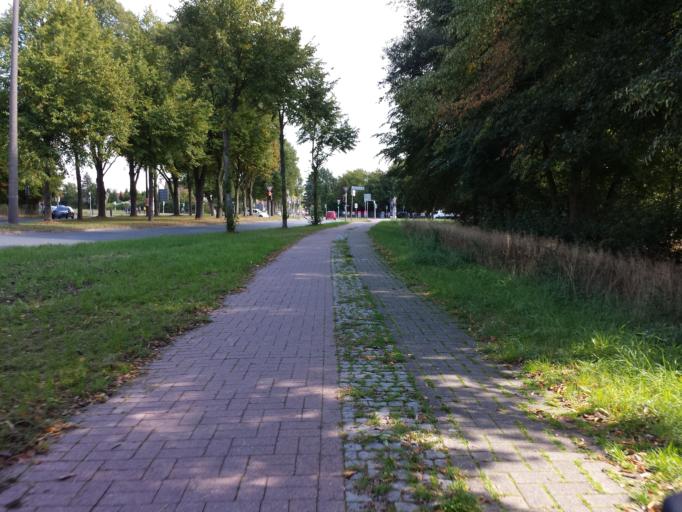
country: DE
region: Bremen
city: Bremen
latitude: 53.0502
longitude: 8.8461
